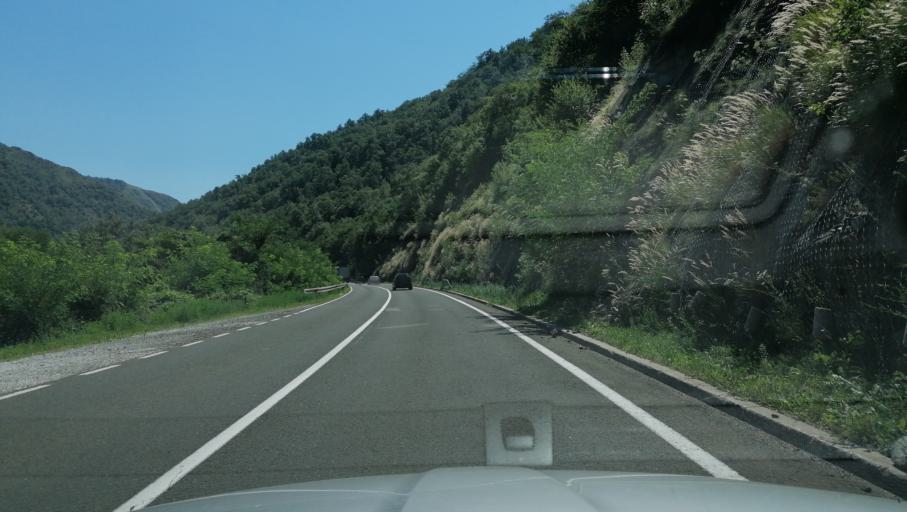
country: RS
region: Central Serbia
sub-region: Raski Okrug
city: Kraljevo
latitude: 43.5911
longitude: 20.5718
